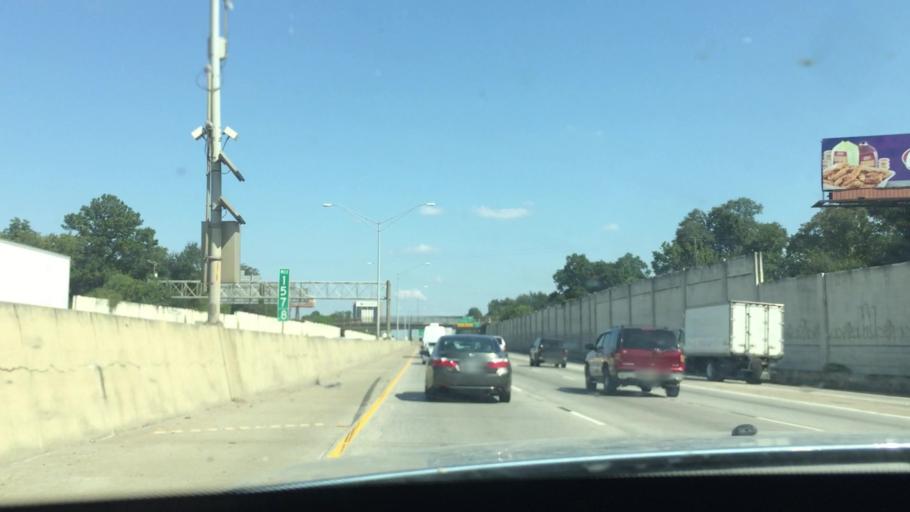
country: US
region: Louisiana
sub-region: East Baton Rouge Parish
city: Baton Rouge
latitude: 30.4239
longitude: -91.1489
